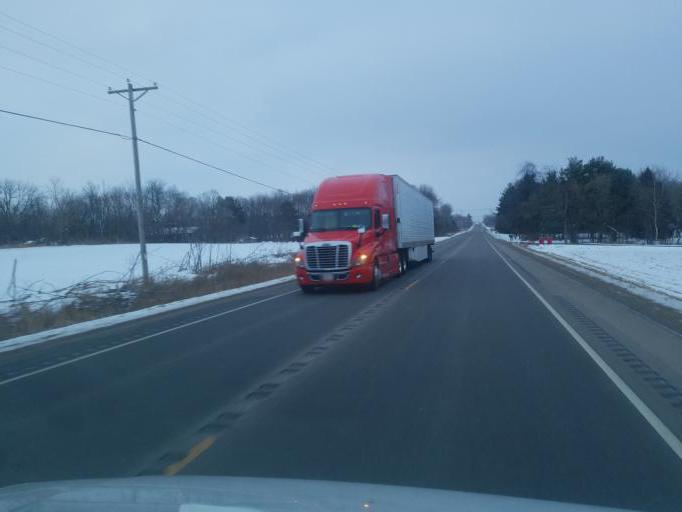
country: US
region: Wisconsin
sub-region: Waupaca County
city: New London
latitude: 44.4098
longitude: -88.8094
